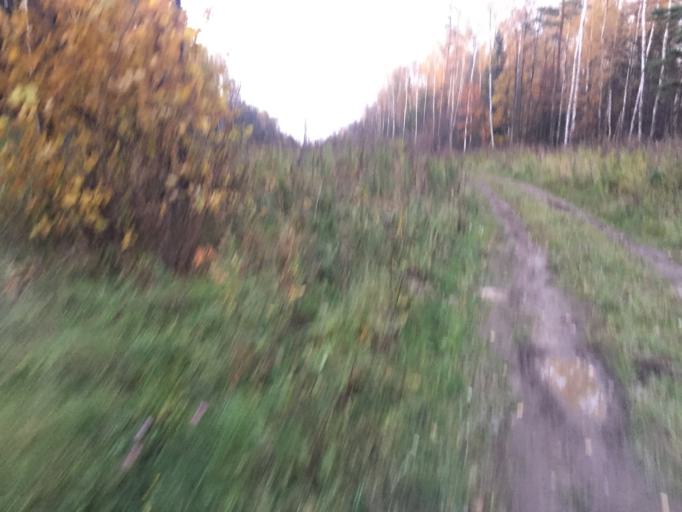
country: RU
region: Moskovskaya
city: Druzhba
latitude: 55.8682
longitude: 37.7676
